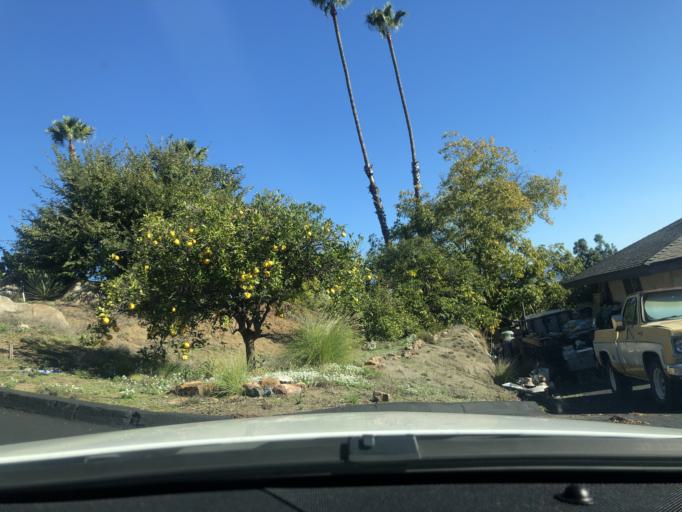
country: US
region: California
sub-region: San Diego County
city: Casa de Oro-Mount Helix
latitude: 32.7692
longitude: -116.9511
